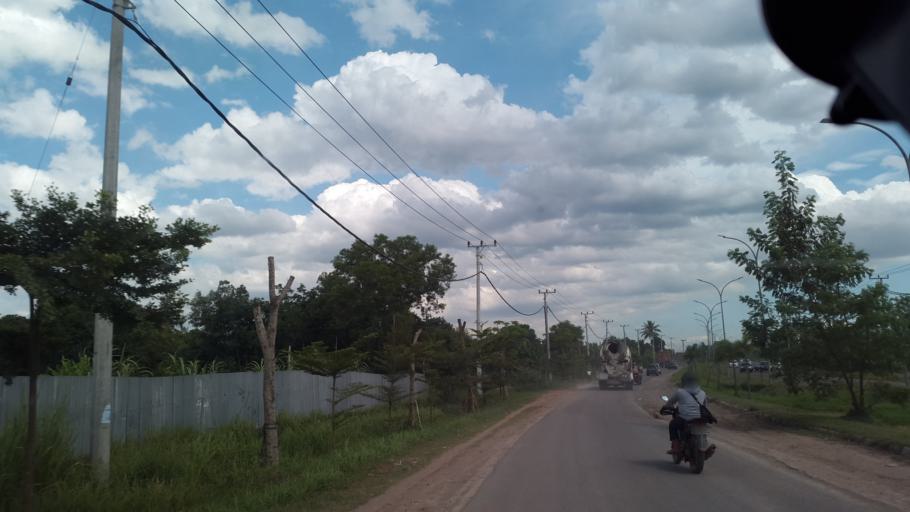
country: ID
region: South Sumatra
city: Palembang
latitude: -2.9056
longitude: 104.7351
